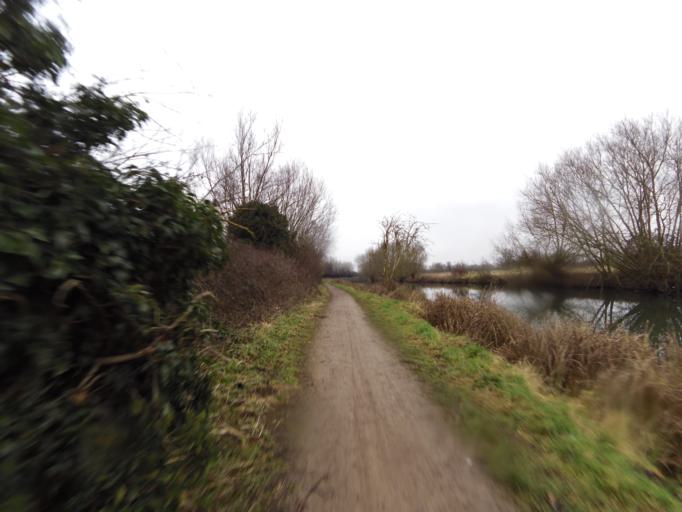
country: GB
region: England
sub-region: Cambridgeshire
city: Waterbeach
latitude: 52.2469
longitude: 0.1849
